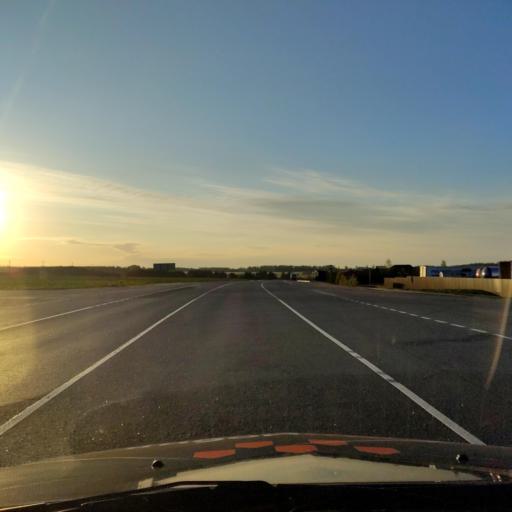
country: RU
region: Orjol
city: Livny
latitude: 52.4499
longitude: 37.5039
